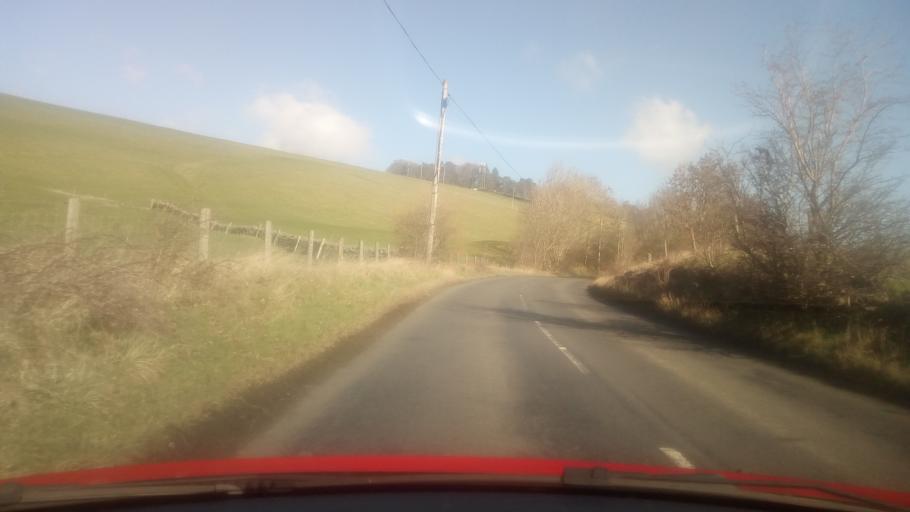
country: GB
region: Scotland
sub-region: The Scottish Borders
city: Selkirk
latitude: 55.5585
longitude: -2.8445
